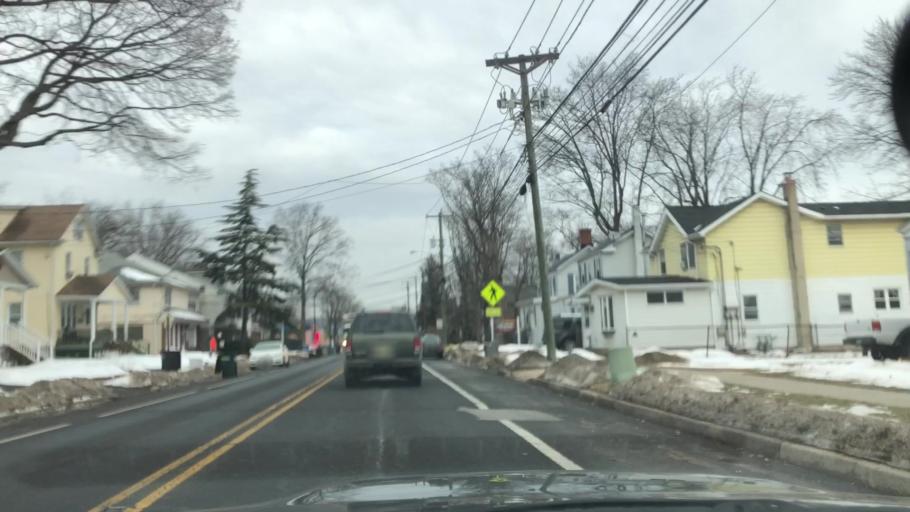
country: US
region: New Jersey
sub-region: Somerset County
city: South Bound Brook
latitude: 40.5522
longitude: -74.5238
